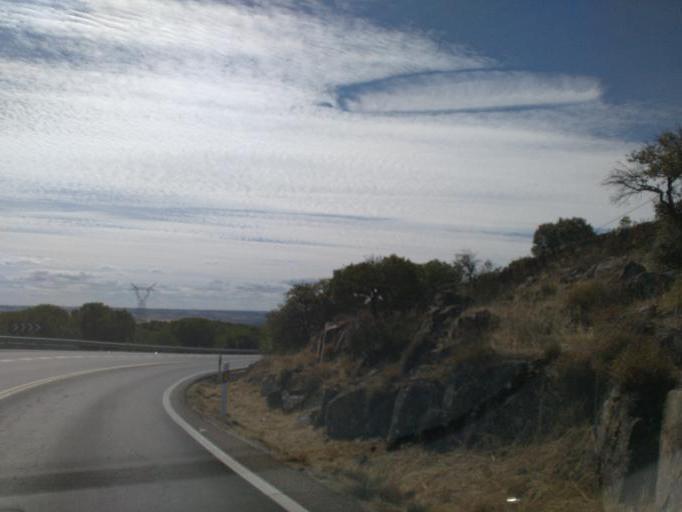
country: ES
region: Madrid
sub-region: Provincia de Madrid
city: Torrelodones
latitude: 40.5521
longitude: -3.9578
